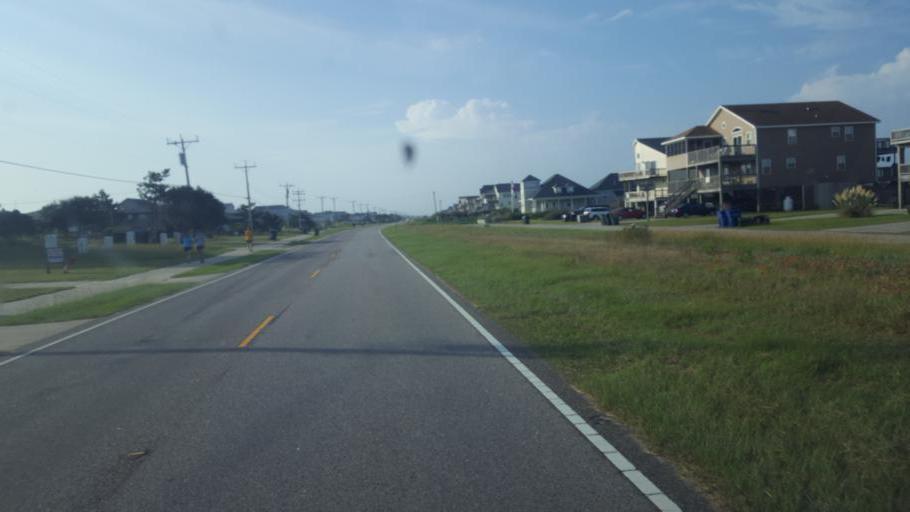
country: US
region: North Carolina
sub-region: Dare County
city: Wanchese
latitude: 35.8879
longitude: -75.5858
